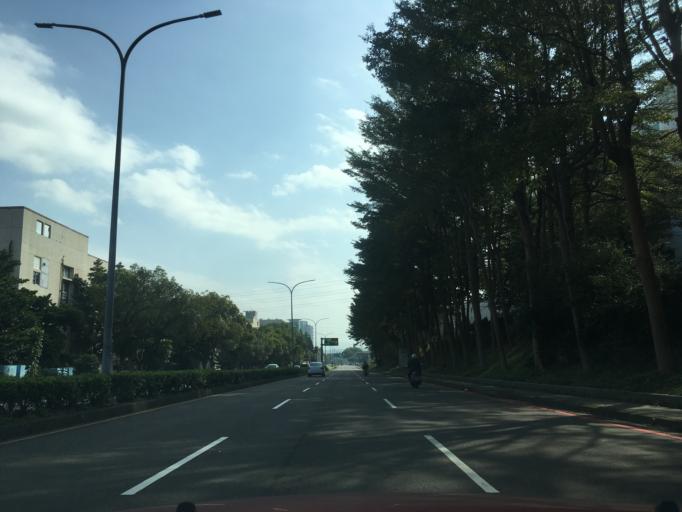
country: TW
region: Taiwan
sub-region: Hsinchu
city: Hsinchu
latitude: 24.7824
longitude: 120.9990
